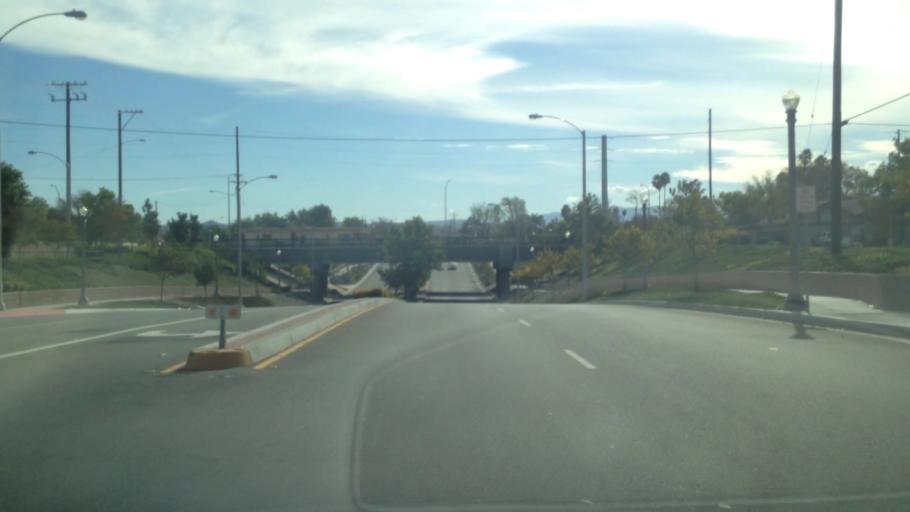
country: US
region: California
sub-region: Riverside County
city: Riverside
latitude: 33.9583
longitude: -117.4187
